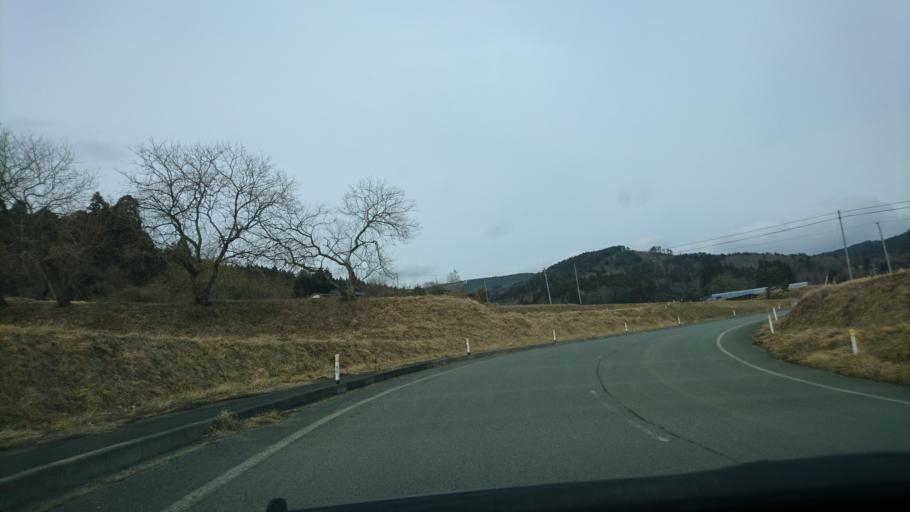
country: JP
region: Iwate
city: Ichinoseki
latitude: 38.8453
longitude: 141.3861
